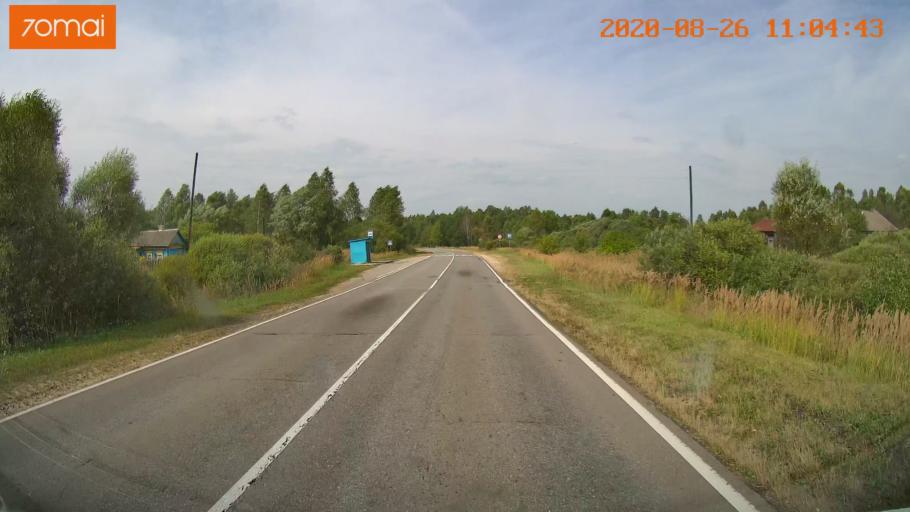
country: RU
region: Rjazan
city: Izhevskoye
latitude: 54.5292
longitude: 41.1897
